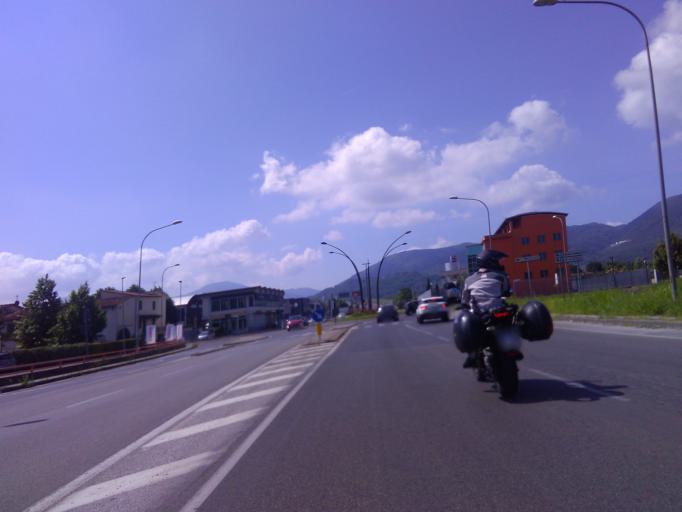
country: IT
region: Tuscany
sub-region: Provincia di Lucca
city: Lucca
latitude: 43.8423
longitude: 10.4765
